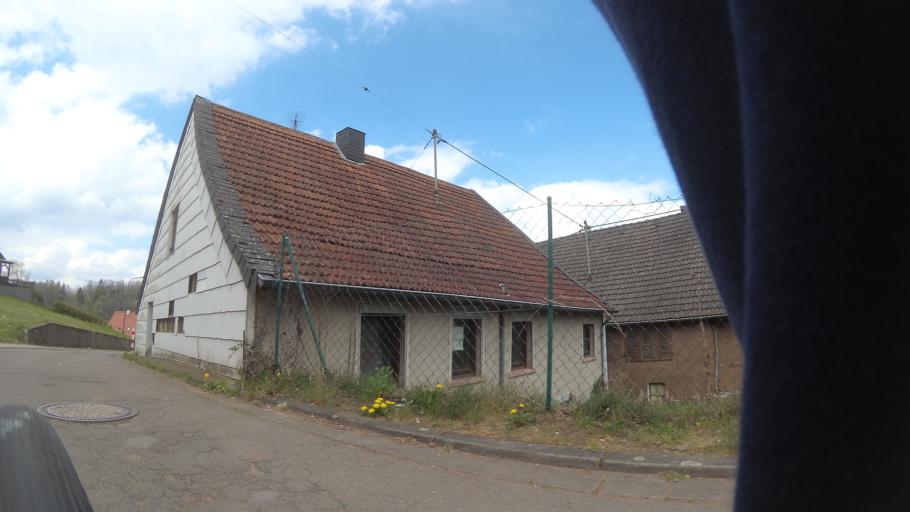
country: DE
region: Saarland
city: Wadern
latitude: 49.5248
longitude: 6.9383
